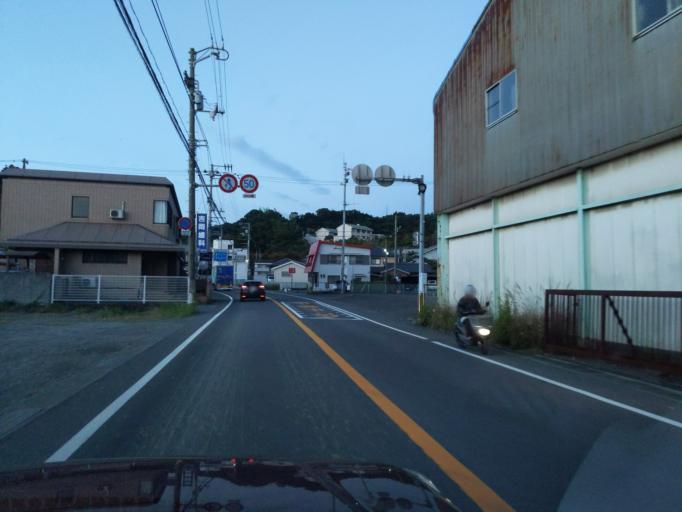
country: JP
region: Tokushima
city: Anan
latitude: 33.8723
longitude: 134.6360
